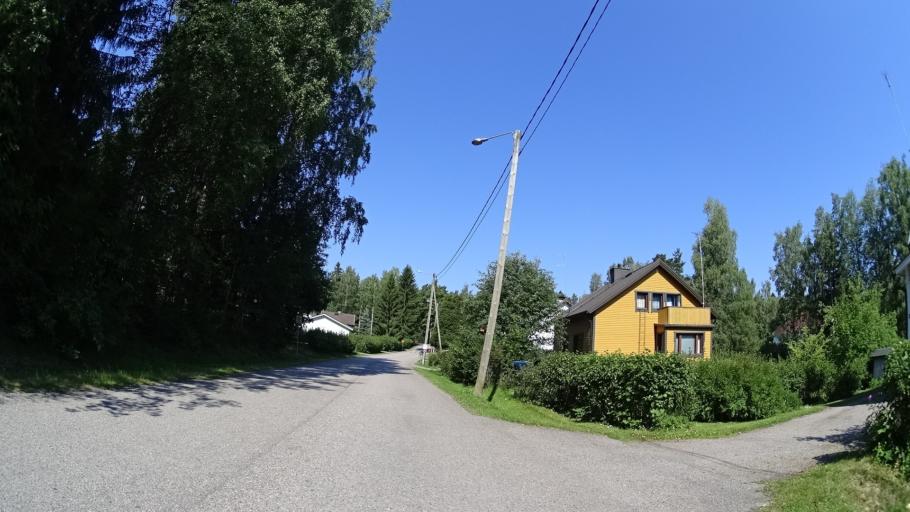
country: FI
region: Uusimaa
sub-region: Helsinki
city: Kerava
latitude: 60.3749
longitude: 25.0821
